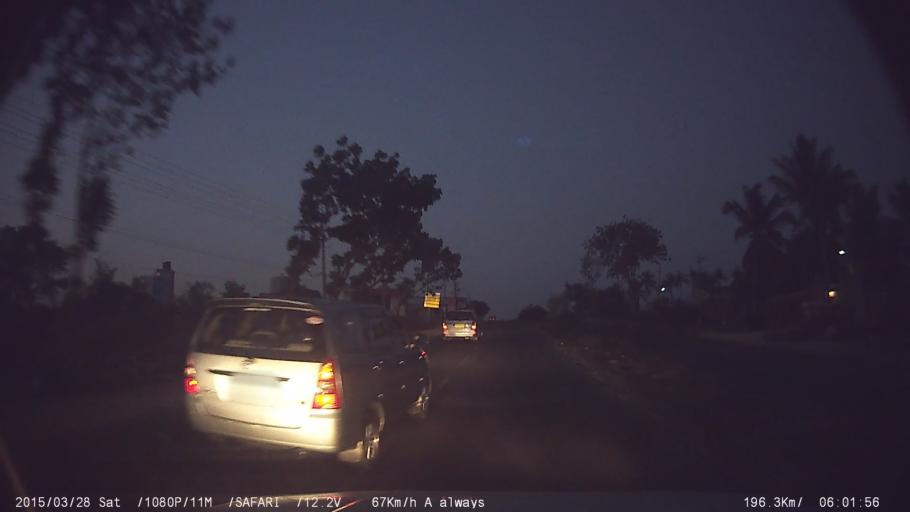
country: IN
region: Karnataka
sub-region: Ramanagara
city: Ramanagaram
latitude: 12.8528
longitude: 77.4257
